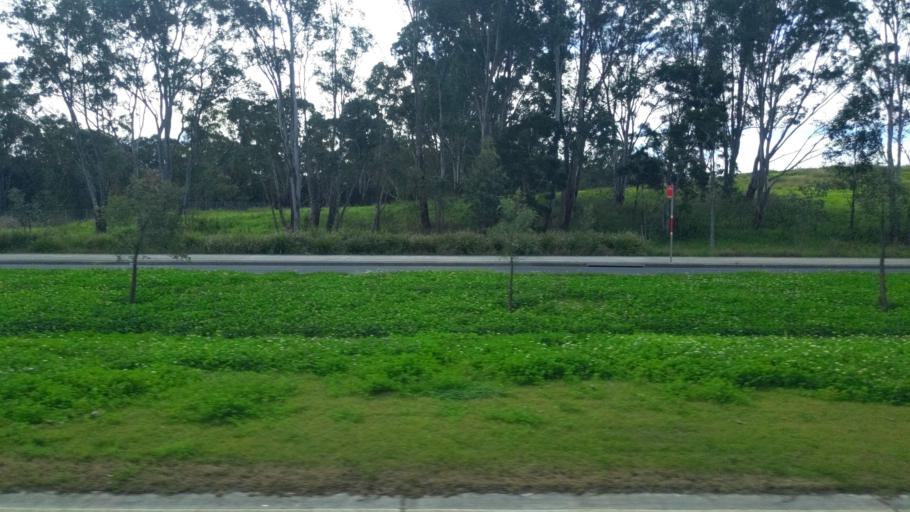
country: AU
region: New South Wales
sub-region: Blacktown
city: Riverstone
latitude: -33.7053
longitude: 150.8500
